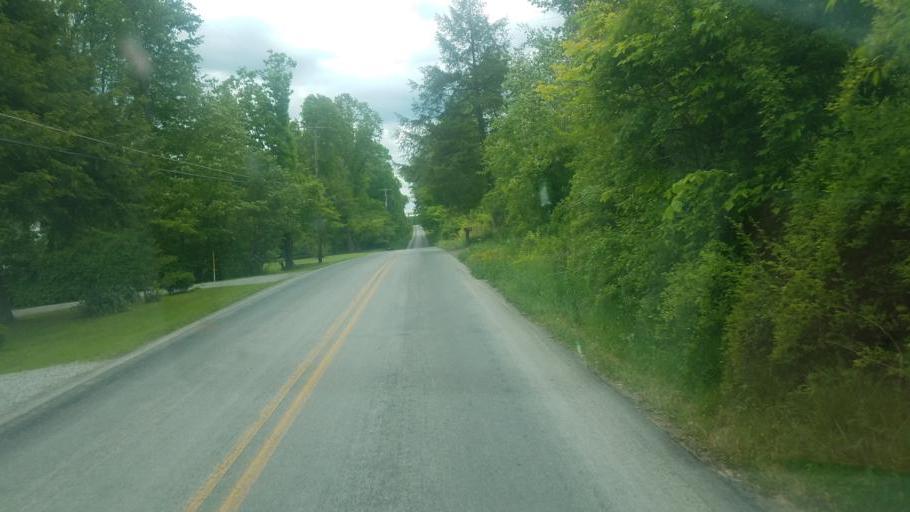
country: US
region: Pennsylvania
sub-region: Venango County
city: Franklin
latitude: 41.2068
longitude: -79.8446
